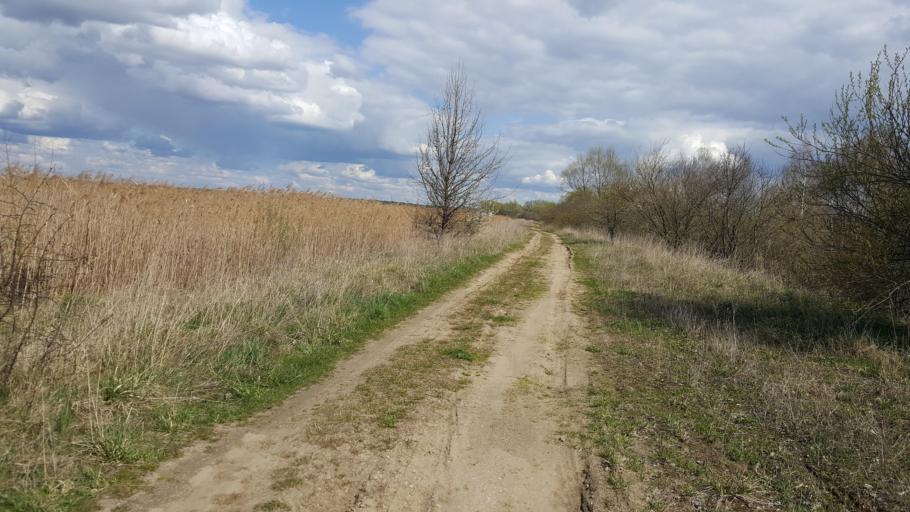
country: BY
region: Brest
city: Kamyanyets
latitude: 52.3724
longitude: 23.6461
